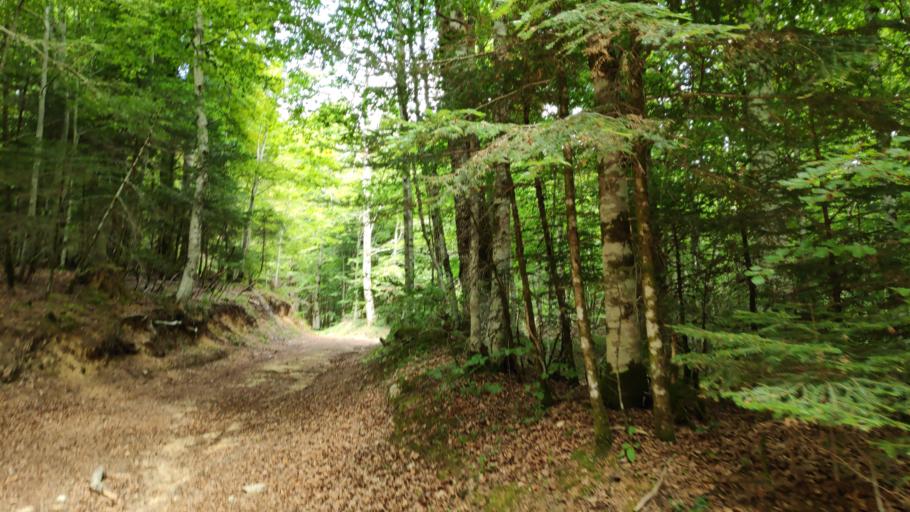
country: IT
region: Calabria
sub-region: Provincia di Vibo-Valentia
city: Mongiana
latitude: 38.5307
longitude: 16.3487
